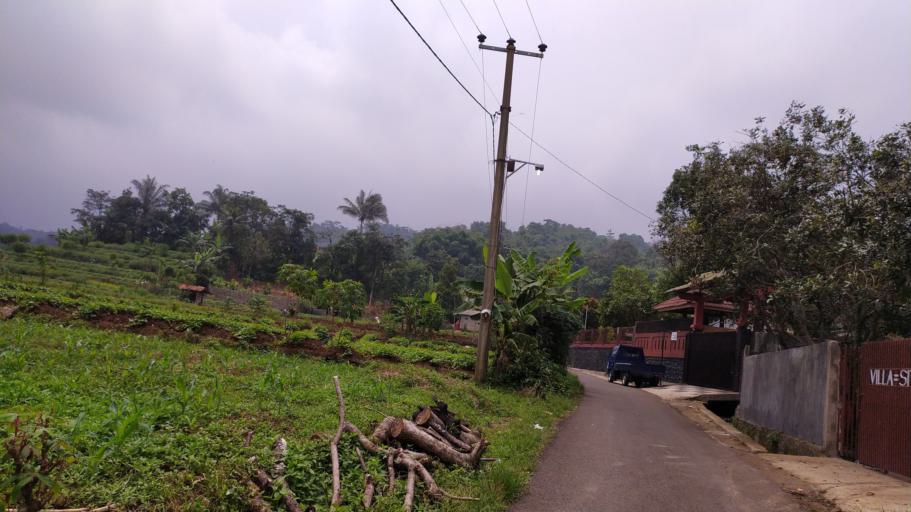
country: ID
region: West Java
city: Ciampea
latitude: -6.6211
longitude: 106.7117
